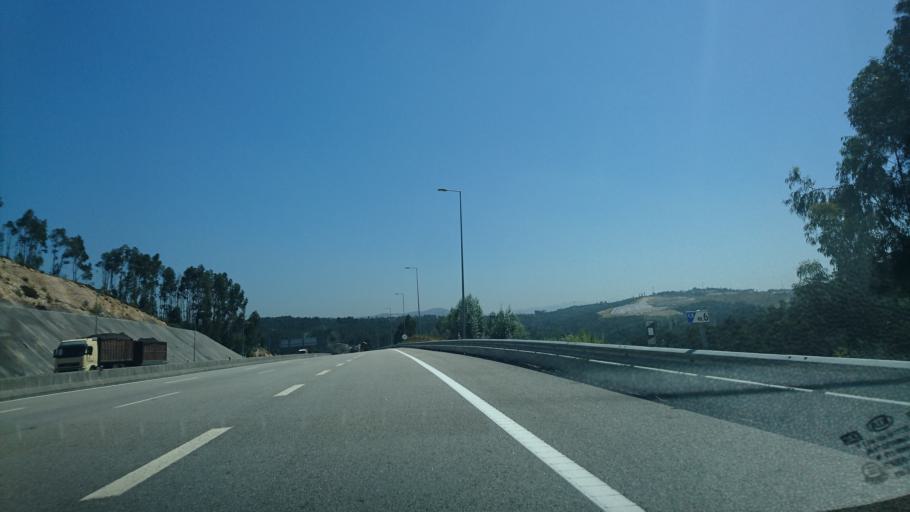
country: PT
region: Porto
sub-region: Vila Nova de Gaia
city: Sandim
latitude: 41.0407
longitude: -8.4894
